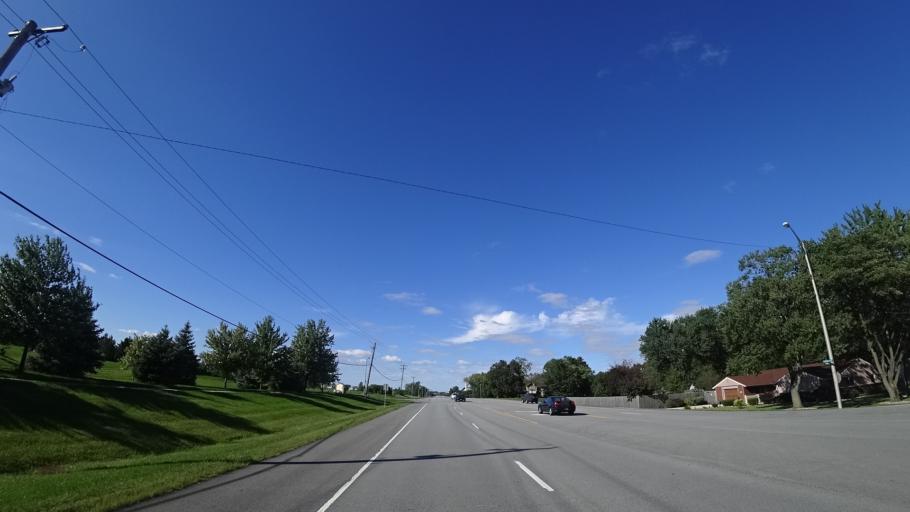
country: US
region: Illinois
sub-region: Cook County
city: Country Club Hills
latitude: 41.5611
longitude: -87.7333
